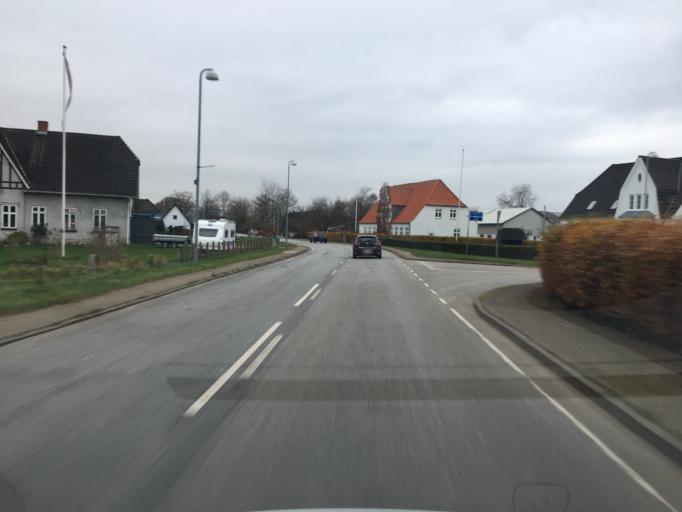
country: DK
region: South Denmark
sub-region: Aabenraa Kommune
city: Tinglev
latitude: 54.9963
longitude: 9.2049
